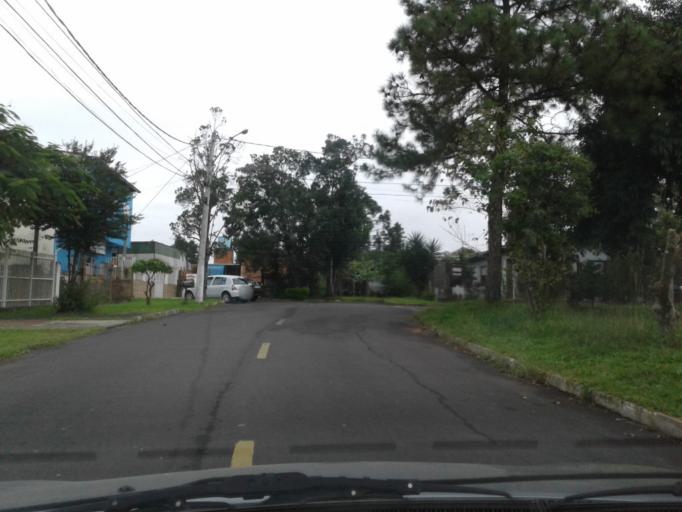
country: BR
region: Rio Grande do Sul
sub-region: Gravatai
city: Gravatai
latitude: -29.9367
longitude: -51.0053
